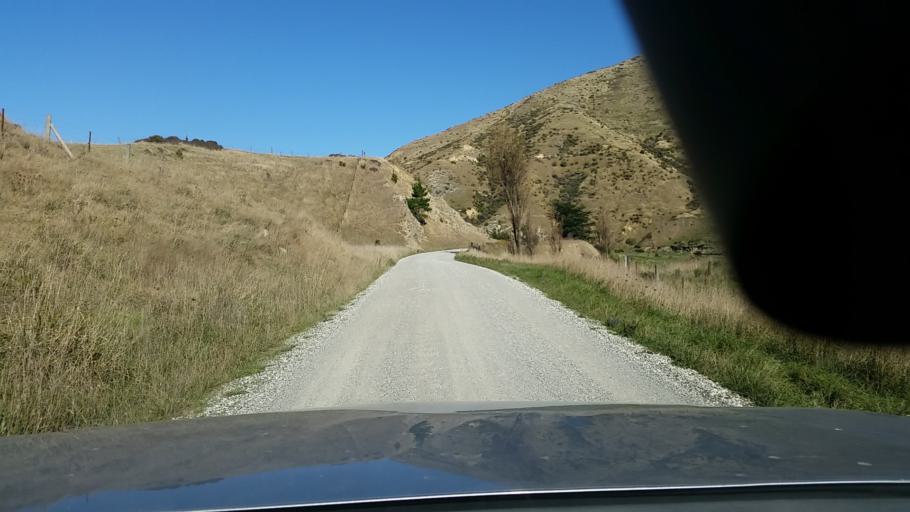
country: NZ
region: Marlborough
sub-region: Marlborough District
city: Blenheim
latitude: -41.8403
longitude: 174.1816
